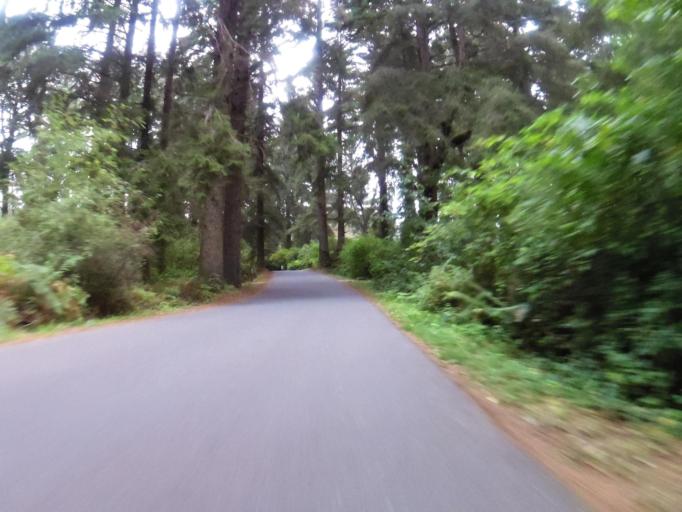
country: US
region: California
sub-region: Humboldt County
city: Westhaven-Moonstone
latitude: 41.1381
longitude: -124.1587
